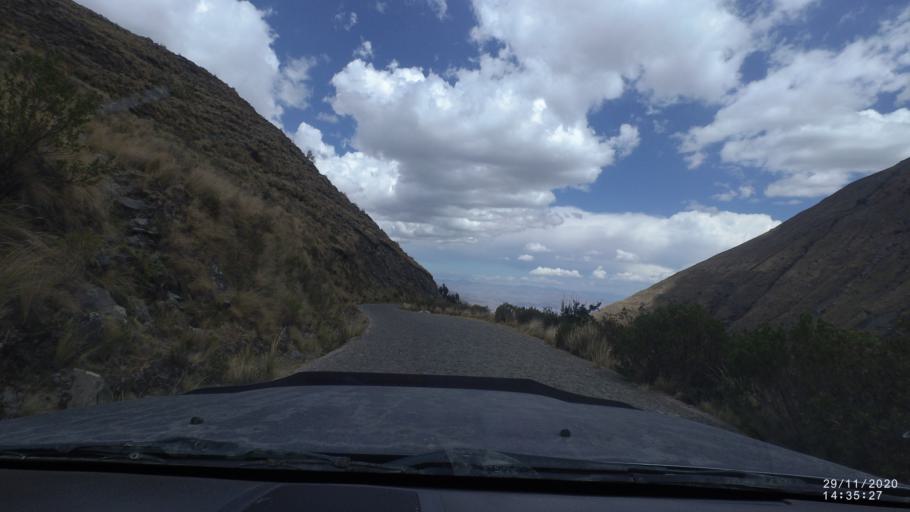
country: BO
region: Cochabamba
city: Sipe Sipe
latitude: -17.2711
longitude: -66.3366
